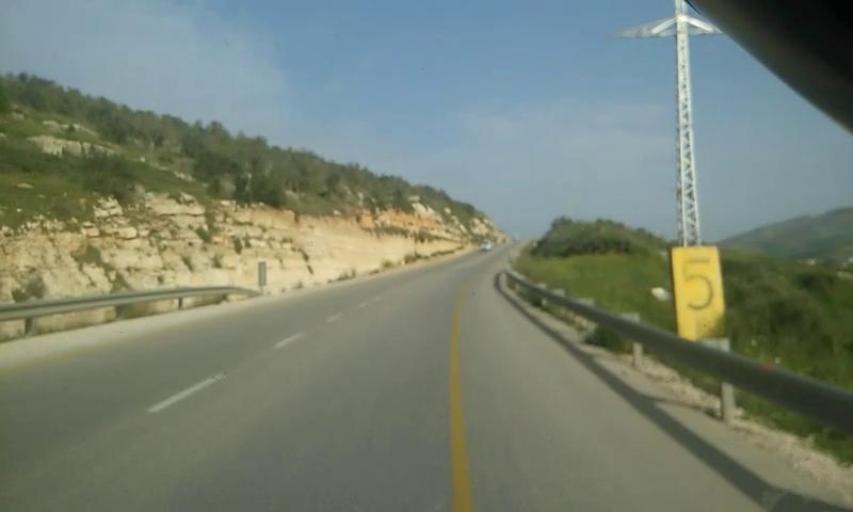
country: PS
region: West Bank
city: Till
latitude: 32.1912
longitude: 35.2035
